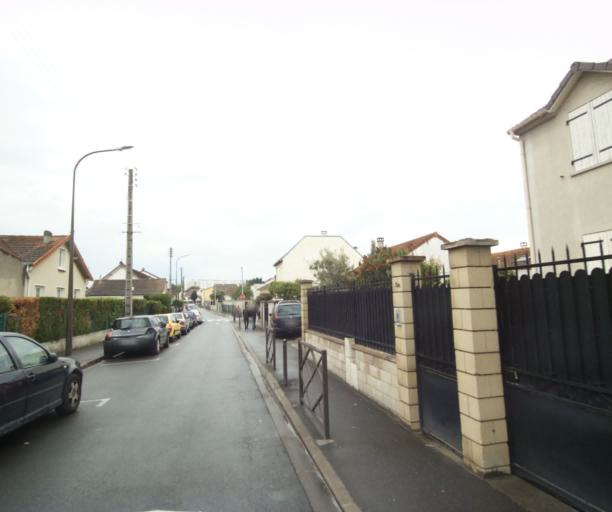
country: FR
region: Ile-de-France
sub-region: Departement du Val-d'Oise
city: Bezons
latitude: 48.9407
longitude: 2.2168
